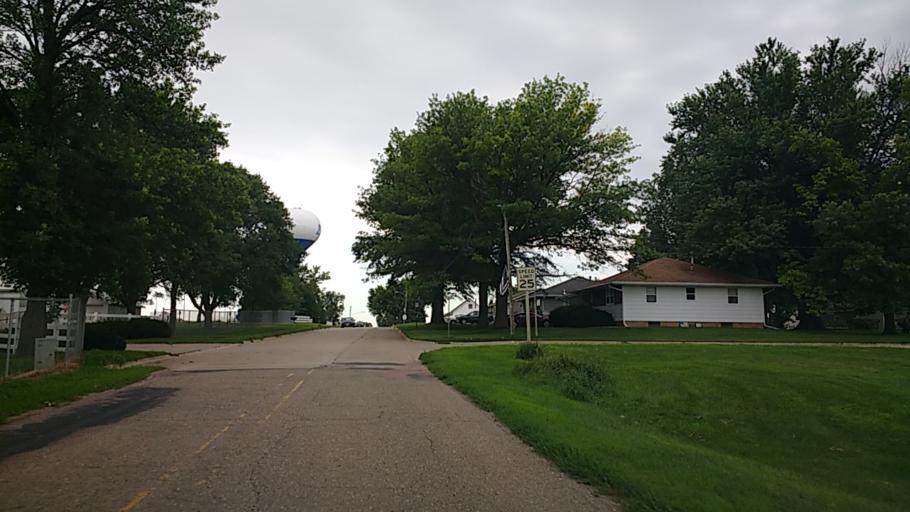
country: US
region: Iowa
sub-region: Woodbury County
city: Moville
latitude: 42.4869
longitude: -96.0654
